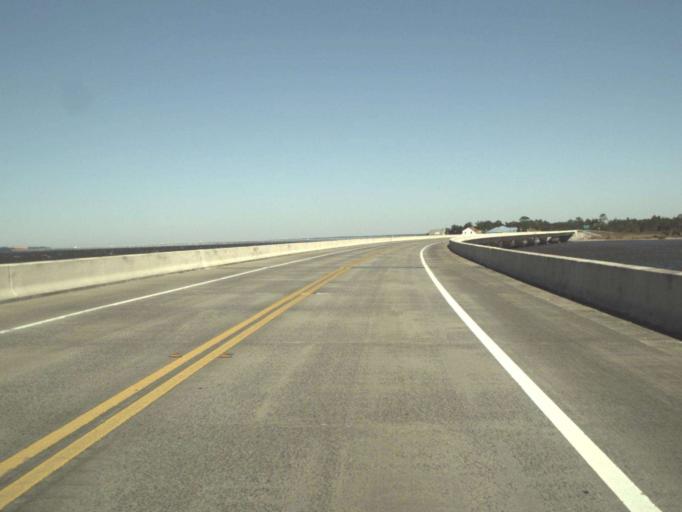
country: US
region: Florida
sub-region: Santa Rosa County
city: Oriole Beach
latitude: 30.4381
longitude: -87.0997
